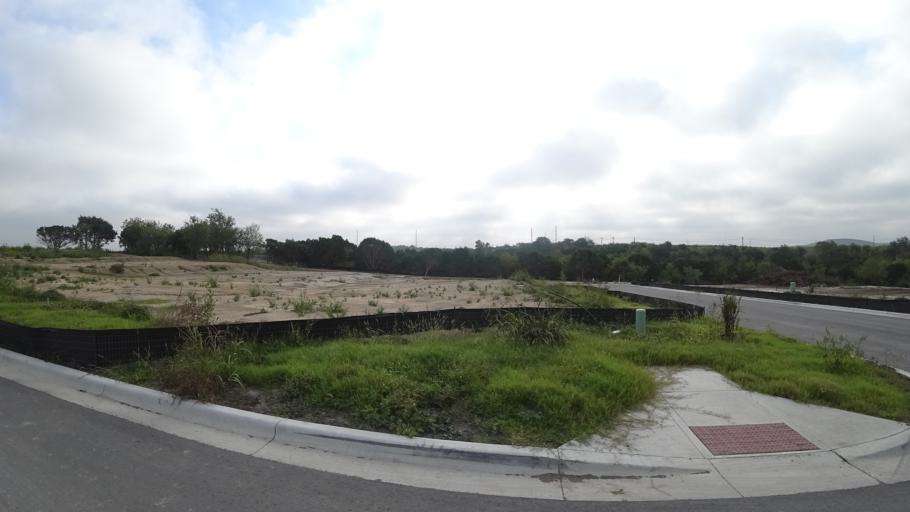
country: US
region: Texas
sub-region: Travis County
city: Manor
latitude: 30.3544
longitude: -97.6431
